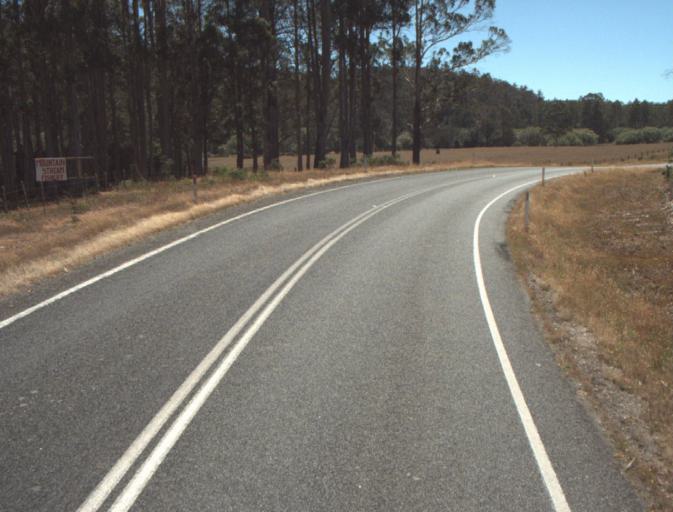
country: AU
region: Tasmania
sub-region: Dorset
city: Scottsdale
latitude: -41.3059
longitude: 147.3818
